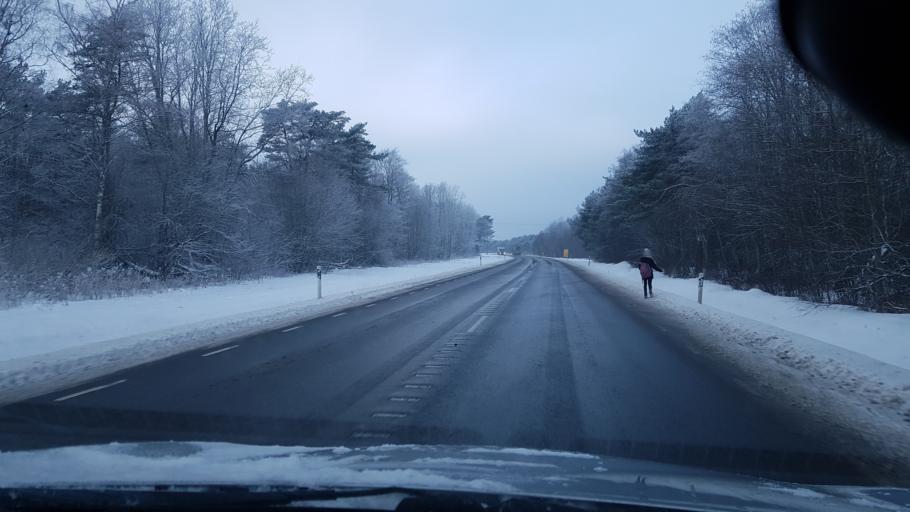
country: EE
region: Harju
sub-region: Paldiski linn
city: Paldiski
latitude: 59.3384
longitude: 24.2208
